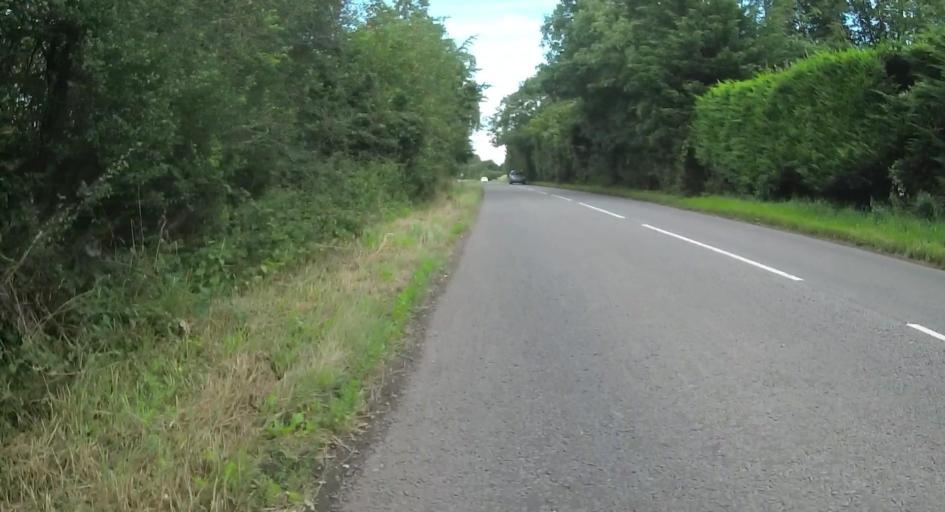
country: GB
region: England
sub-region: Hampshire
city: Overton
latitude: 51.2465
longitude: -1.3340
